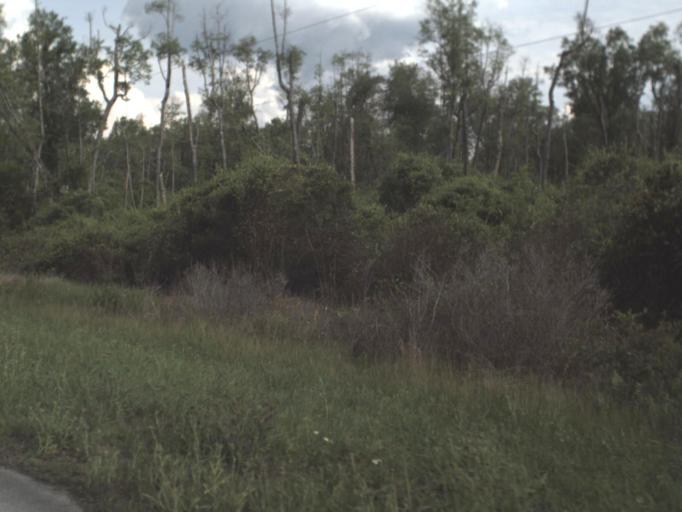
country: US
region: Florida
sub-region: Baker County
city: Macclenny
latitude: 30.5180
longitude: -82.2807
